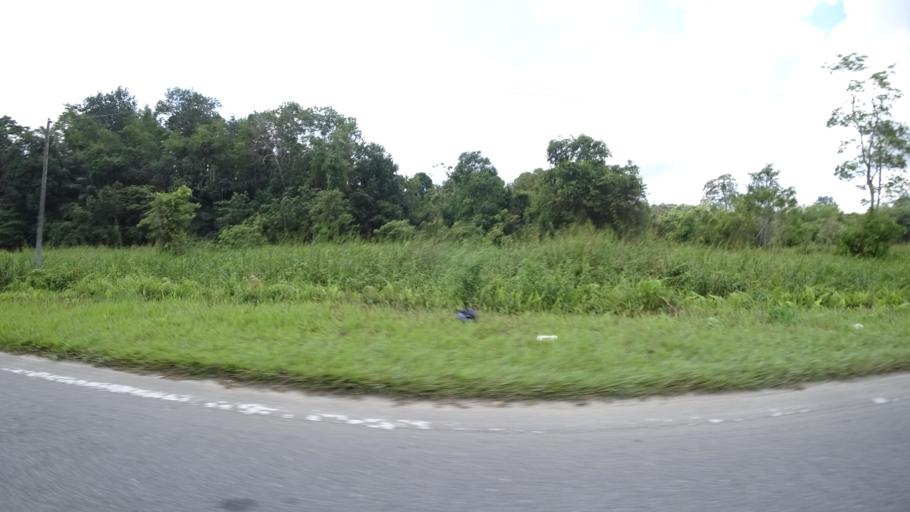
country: BN
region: Tutong
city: Tutong
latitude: 4.6986
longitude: 114.8029
